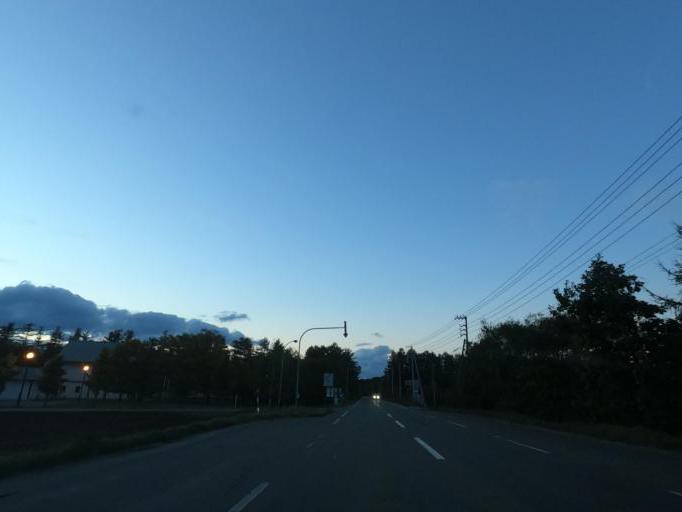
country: JP
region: Hokkaido
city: Obihiro
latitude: 42.6728
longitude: 143.1685
